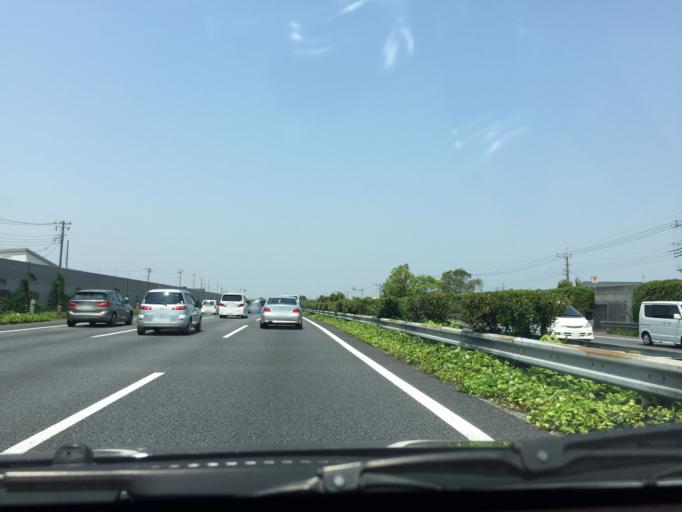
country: JP
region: Saitama
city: Kazo
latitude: 36.1316
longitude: 139.6223
